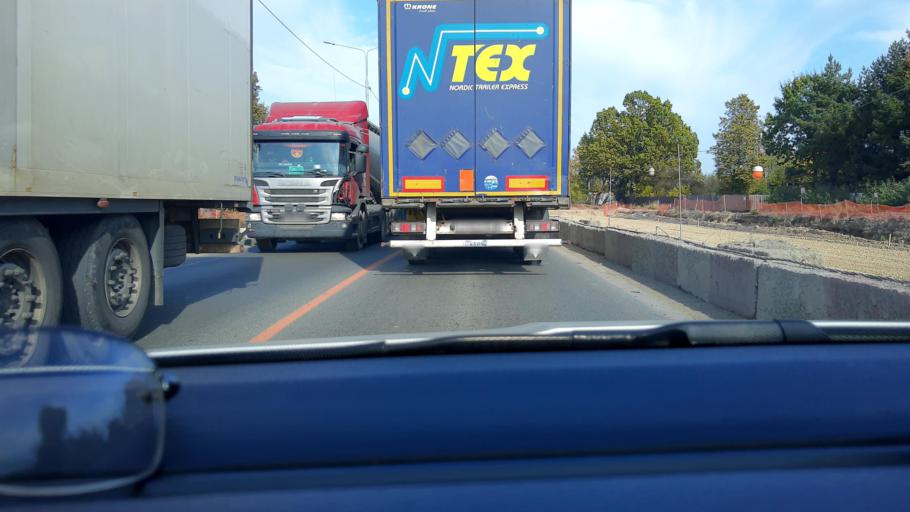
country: RU
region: Moskovskaya
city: Selyatino
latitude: 55.5344
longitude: 36.9829
